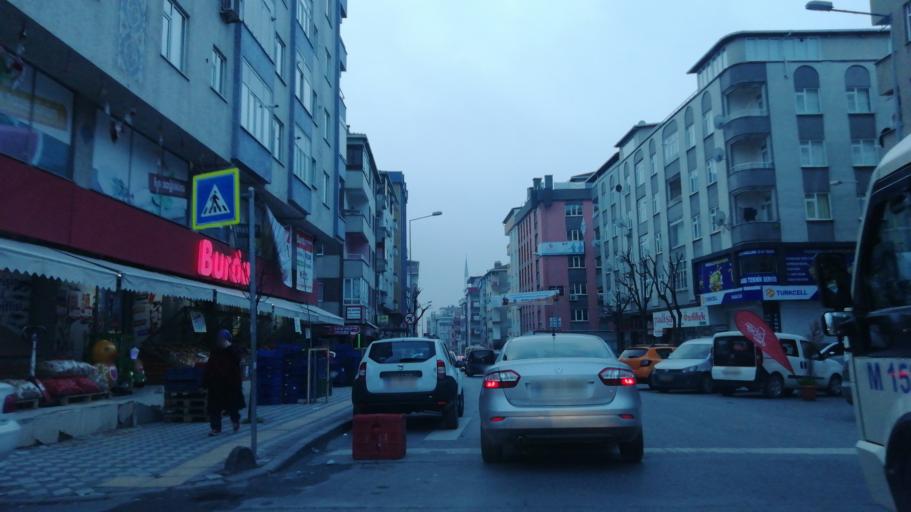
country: TR
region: Istanbul
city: Bahcelievler
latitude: 41.0018
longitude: 28.8302
